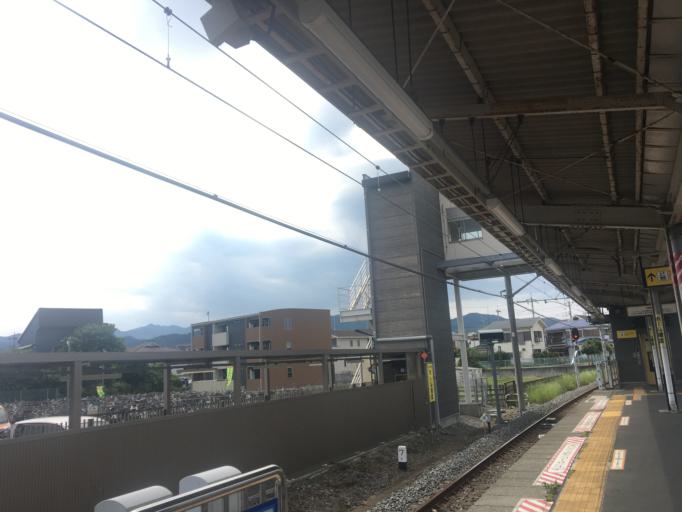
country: JP
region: Saitama
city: Morohongo
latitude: 35.9471
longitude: 139.3153
